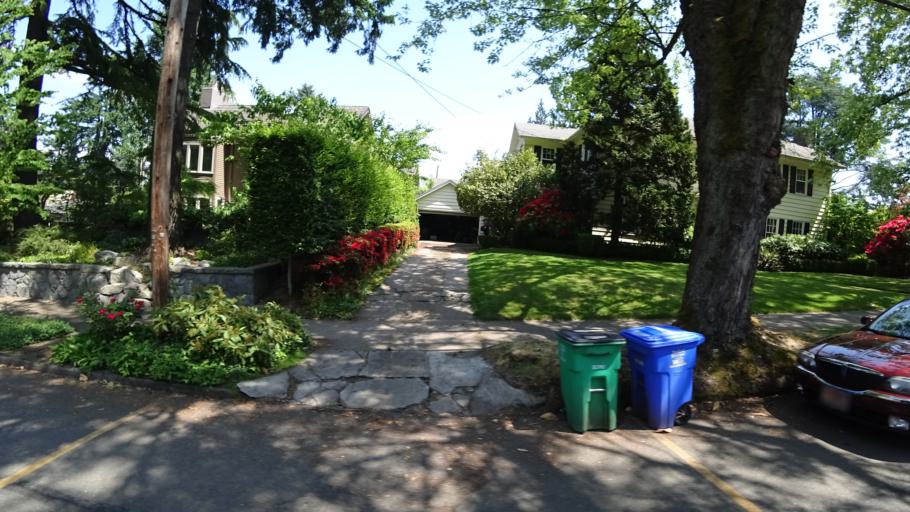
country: US
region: Oregon
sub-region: Multnomah County
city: Portland
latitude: 45.5227
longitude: -122.7067
